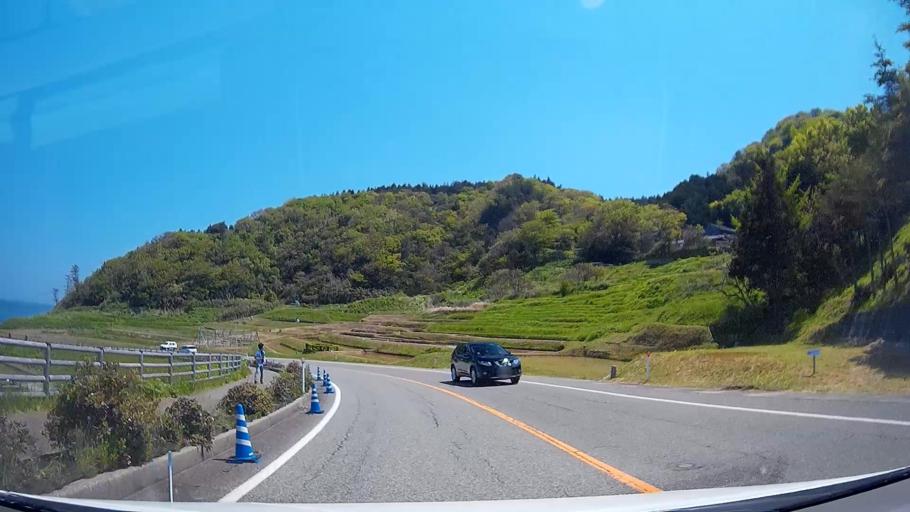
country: JP
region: Ishikawa
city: Nanao
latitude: 37.4246
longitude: 136.9990
